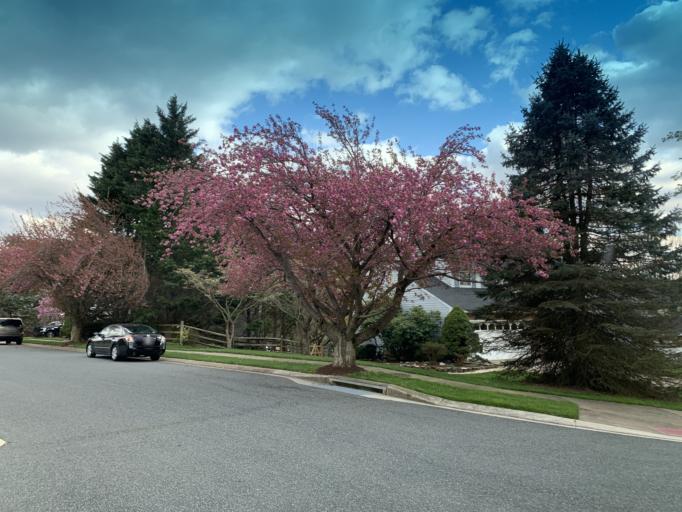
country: US
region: Maryland
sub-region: Harford County
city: South Bel Air
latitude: 39.5445
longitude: -76.3167
